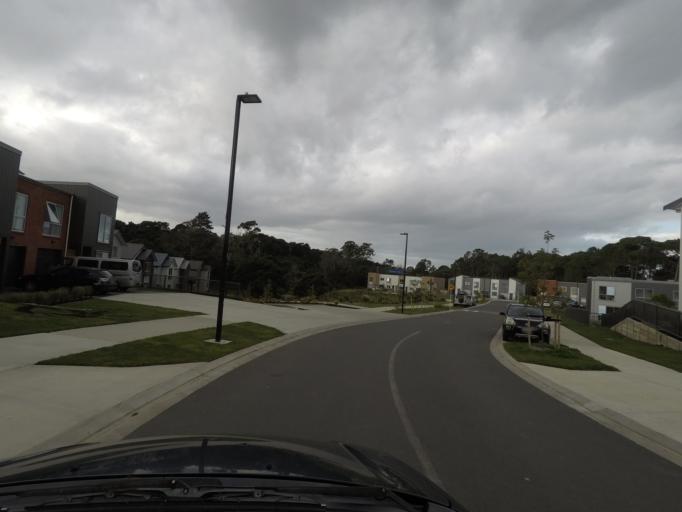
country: NZ
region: Auckland
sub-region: Auckland
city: Rosebank
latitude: -36.8264
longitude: 174.6268
